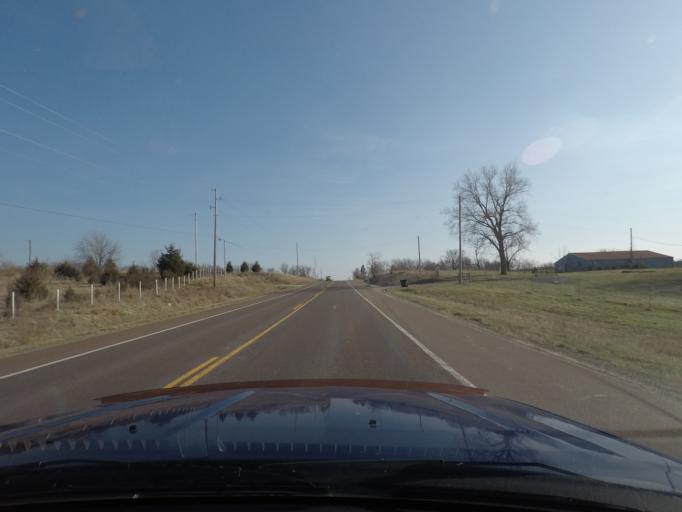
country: US
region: Kansas
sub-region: Douglas County
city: Lawrence
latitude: 39.0176
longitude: -95.3914
